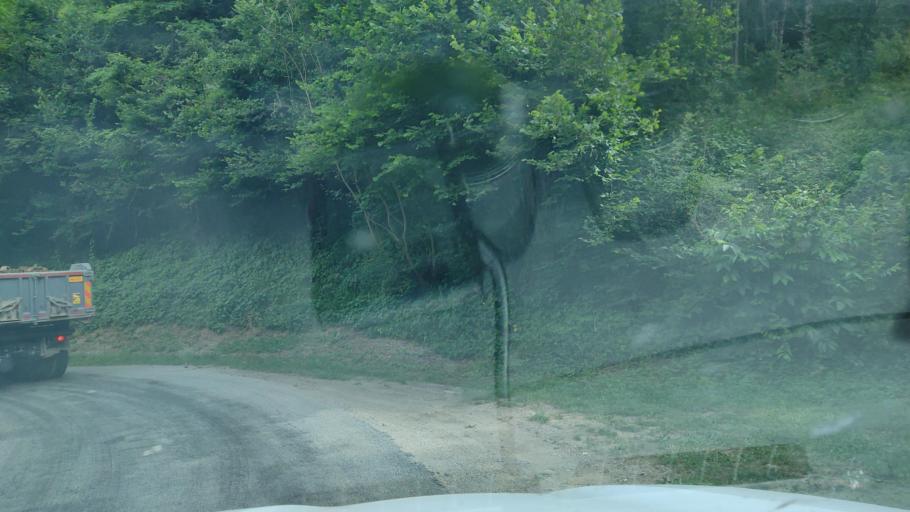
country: FR
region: Rhone-Alpes
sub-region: Departement de la Savoie
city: Barby
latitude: 45.5796
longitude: 6.0412
